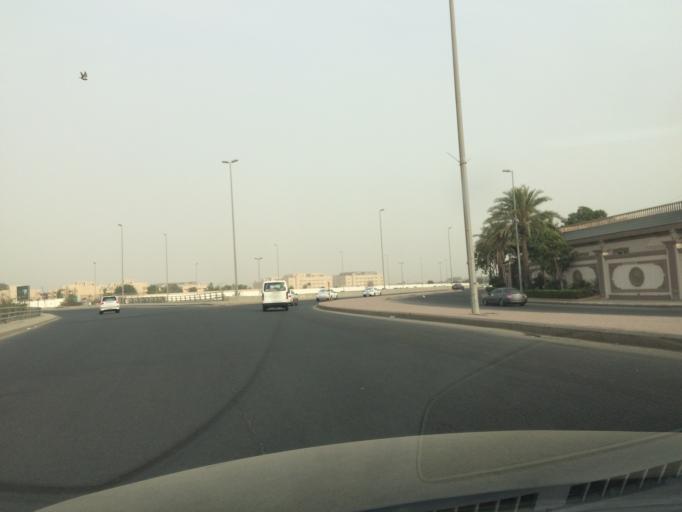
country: SA
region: Makkah
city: Jeddah
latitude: 21.4948
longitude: 39.2284
